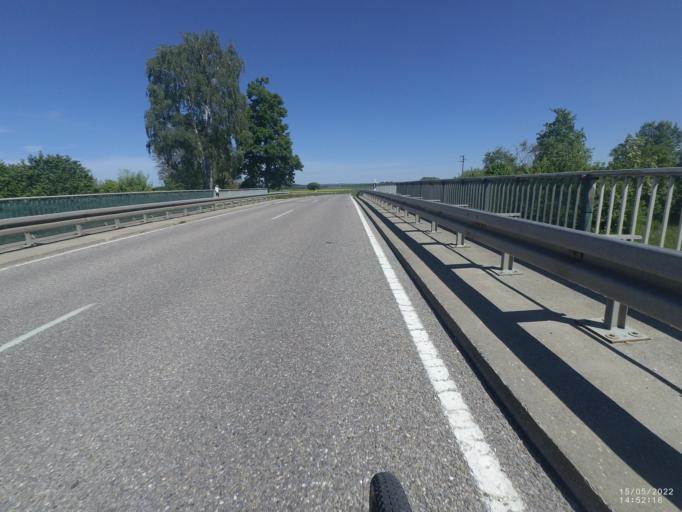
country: DE
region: Baden-Wuerttemberg
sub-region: Regierungsbezirk Stuttgart
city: Bolheim
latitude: 48.6002
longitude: 10.1377
